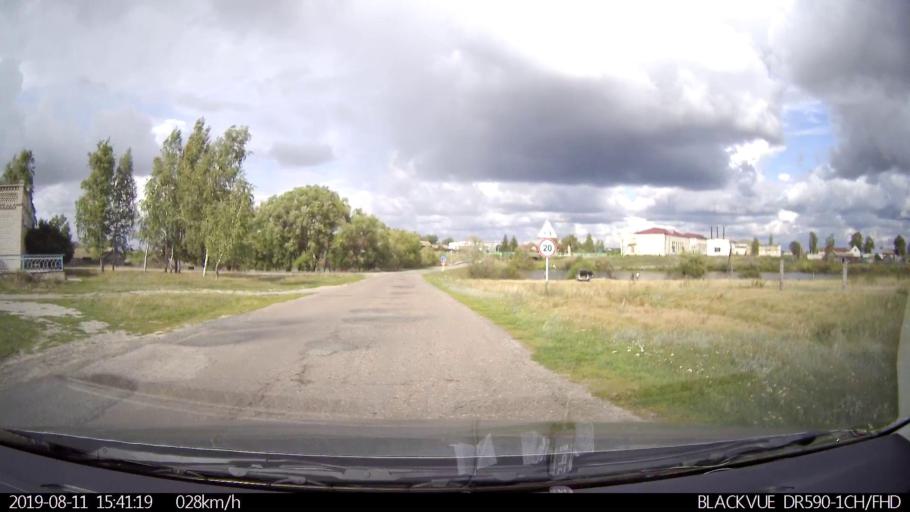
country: RU
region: Ulyanovsk
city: Ignatovka
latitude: 53.8731
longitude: 47.6489
